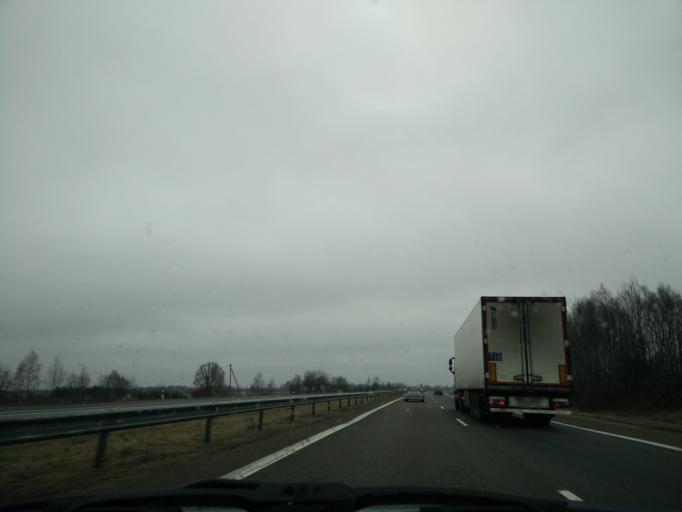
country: LT
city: Skaudvile
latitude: 55.4216
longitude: 22.7713
